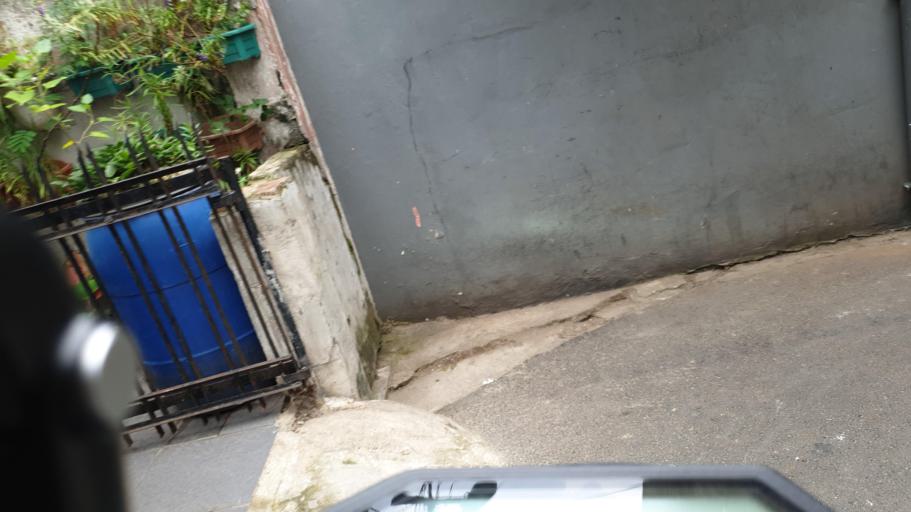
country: ID
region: Banten
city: South Tangerang
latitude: -6.2718
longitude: 106.7932
